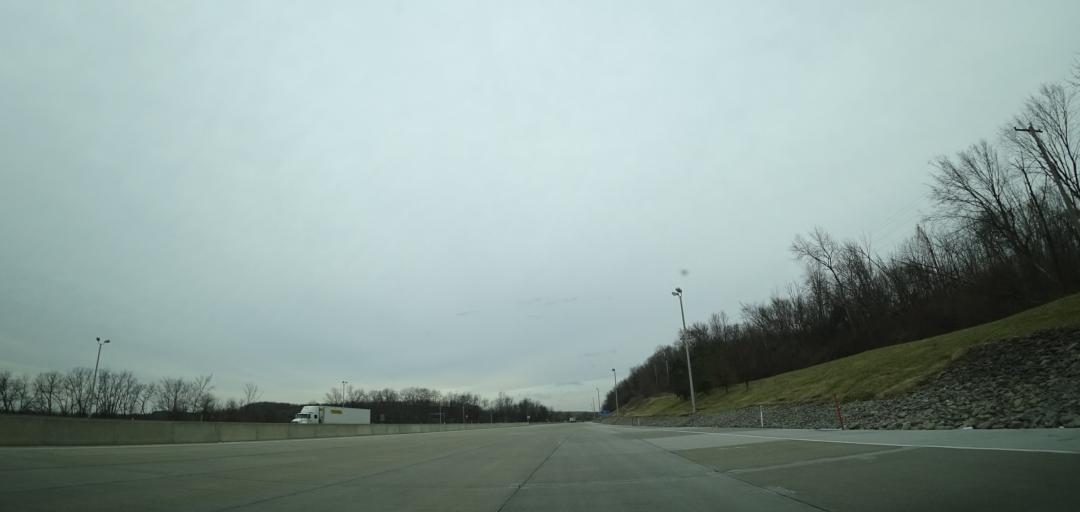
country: US
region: Pennsylvania
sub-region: Lawrence County
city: Bessemer
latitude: 40.9037
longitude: -80.4938
